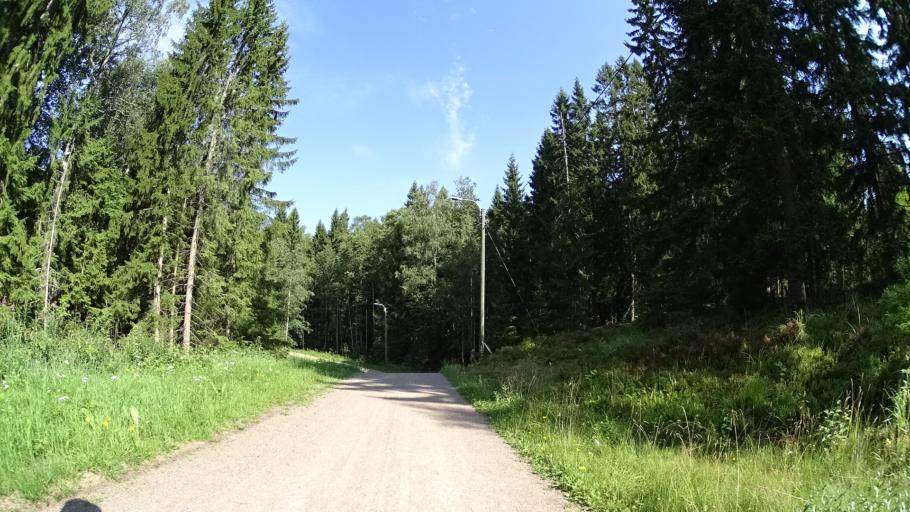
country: FI
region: Uusimaa
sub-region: Helsinki
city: Kilo
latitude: 60.2991
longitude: 24.8147
